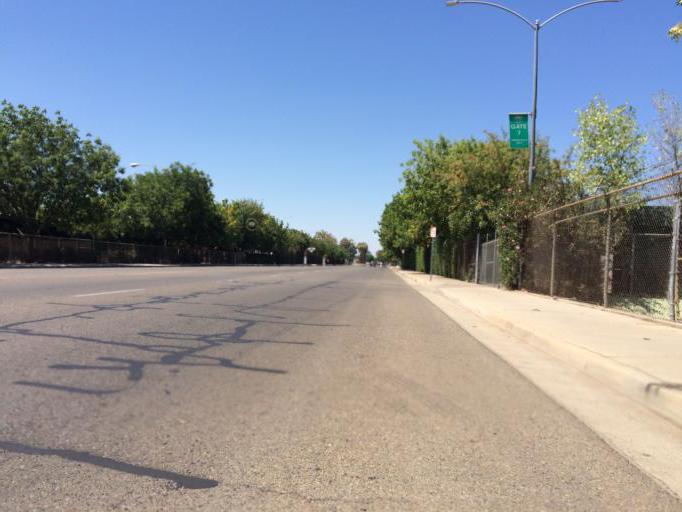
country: US
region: California
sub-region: Fresno County
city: Fresno
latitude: 36.7286
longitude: -119.7478
